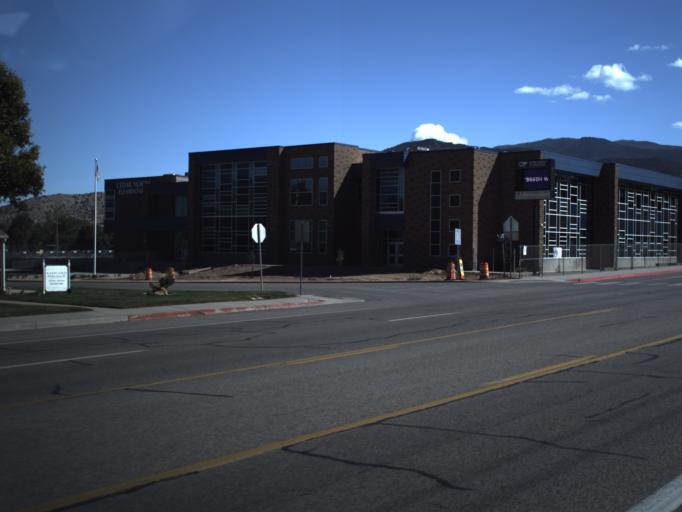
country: US
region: Utah
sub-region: Iron County
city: Cedar City
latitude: 37.6808
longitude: -113.0720
